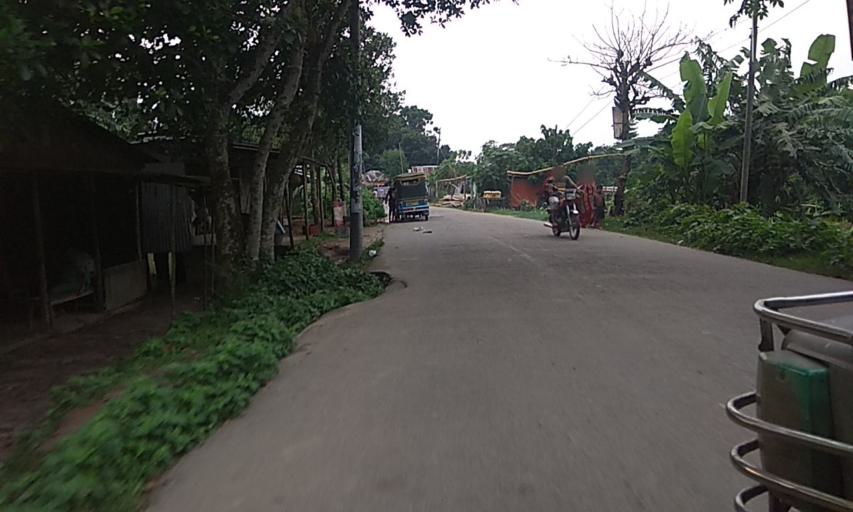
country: BD
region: Dhaka
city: Dohar
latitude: 23.4557
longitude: 90.0058
